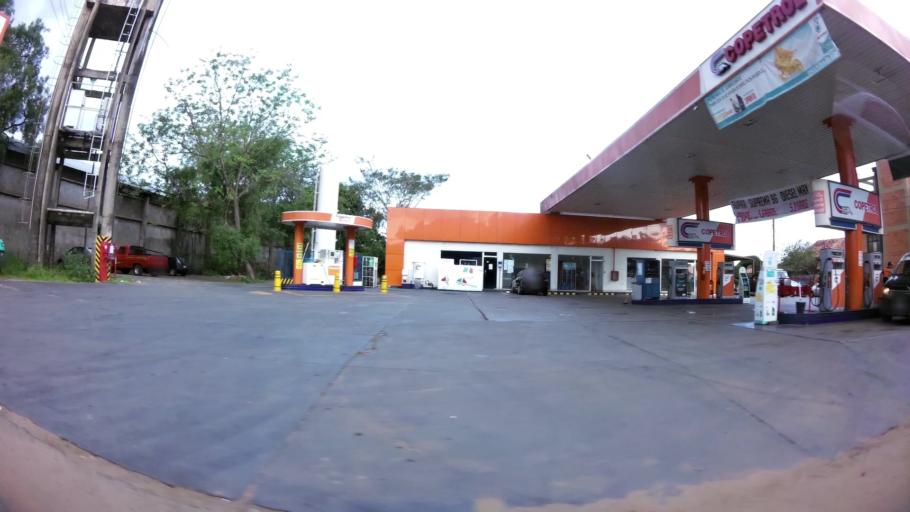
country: PY
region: Central
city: Villa Elisa
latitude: -25.3420
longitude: -57.5663
